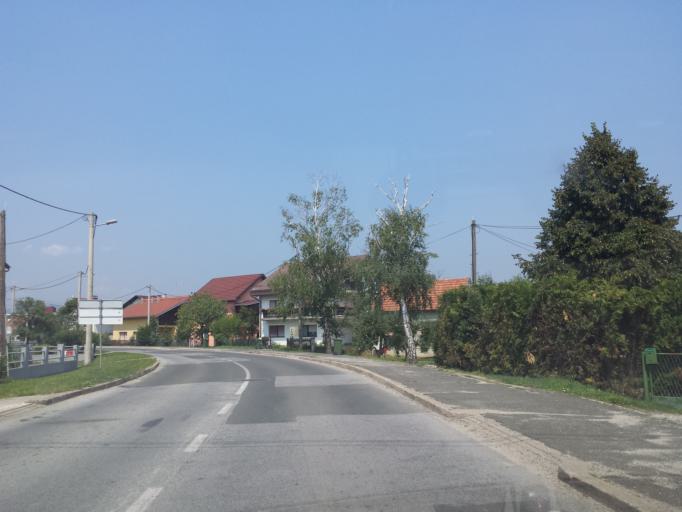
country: HR
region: Zagrebacka
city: Jastrebarsko
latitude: 45.6569
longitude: 15.6432
